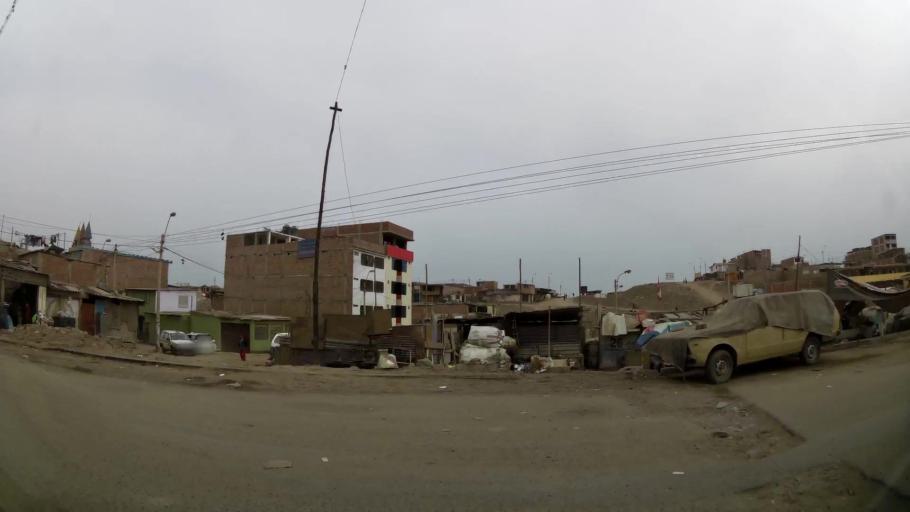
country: PE
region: Lima
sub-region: Lima
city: Surco
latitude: -12.2380
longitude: -76.9372
